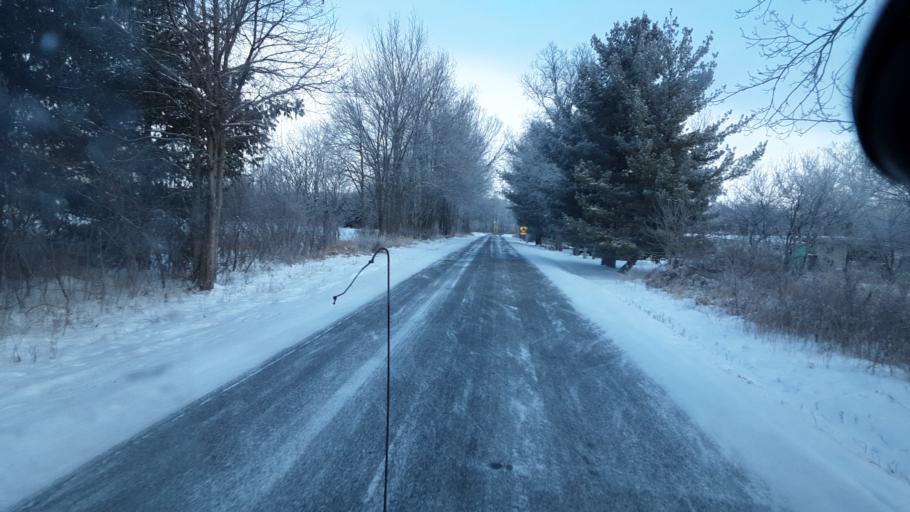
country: US
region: Michigan
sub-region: Ingham County
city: Leslie
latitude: 42.4485
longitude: -84.4970
